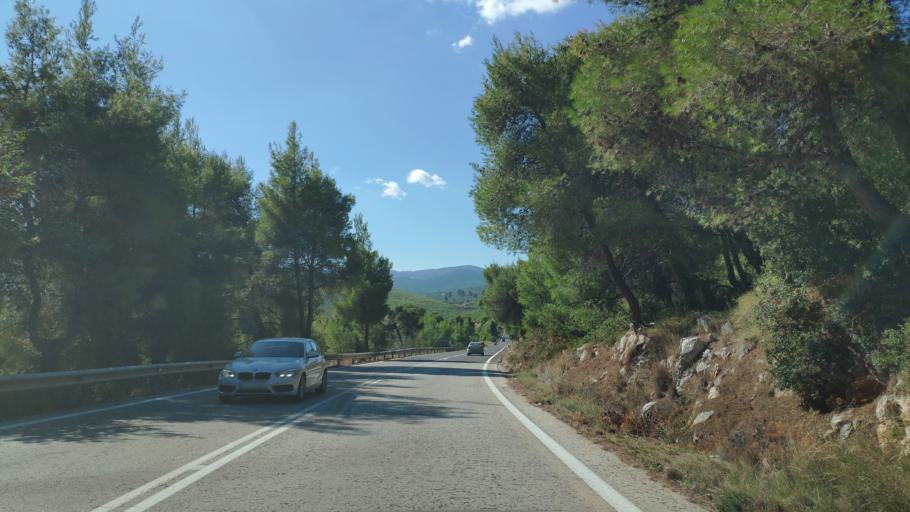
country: GR
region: Peloponnese
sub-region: Nomos Korinthias
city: Sofikon
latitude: 37.8216
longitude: 23.1025
